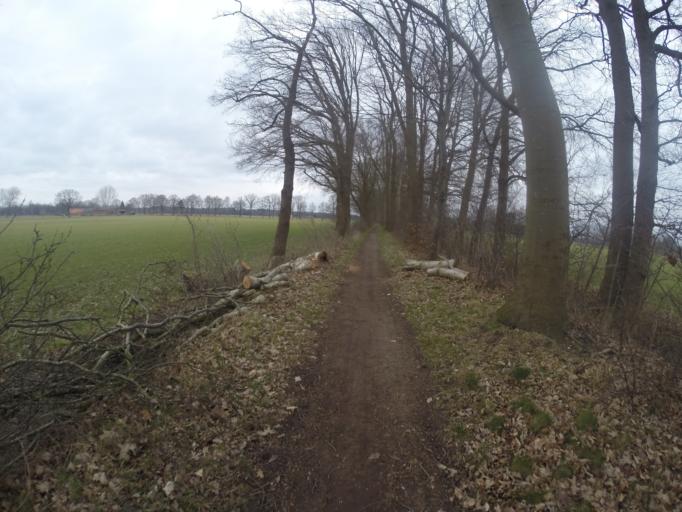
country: NL
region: Gelderland
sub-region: Gemeente Bronckhorst
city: Zelhem
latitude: 52.0188
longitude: 6.3681
